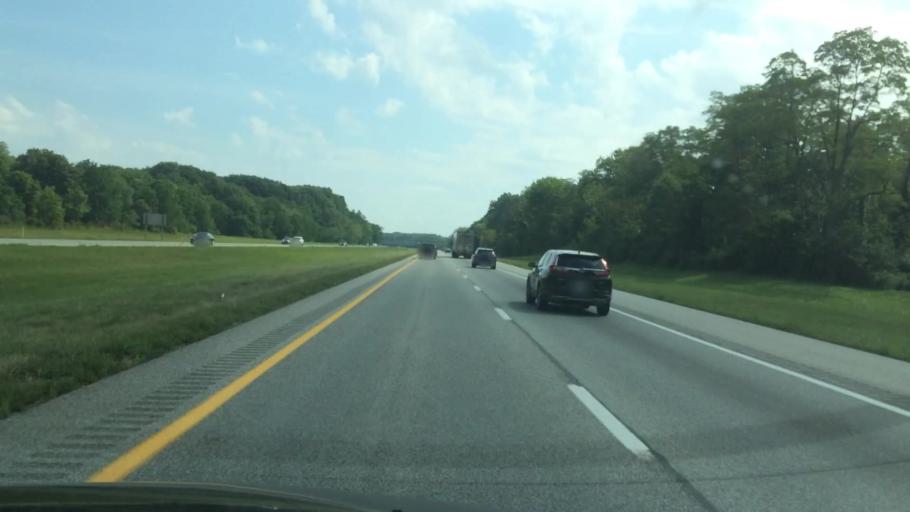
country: US
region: Ohio
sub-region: Lake County
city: Madison
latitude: 41.7626
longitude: -81.0150
